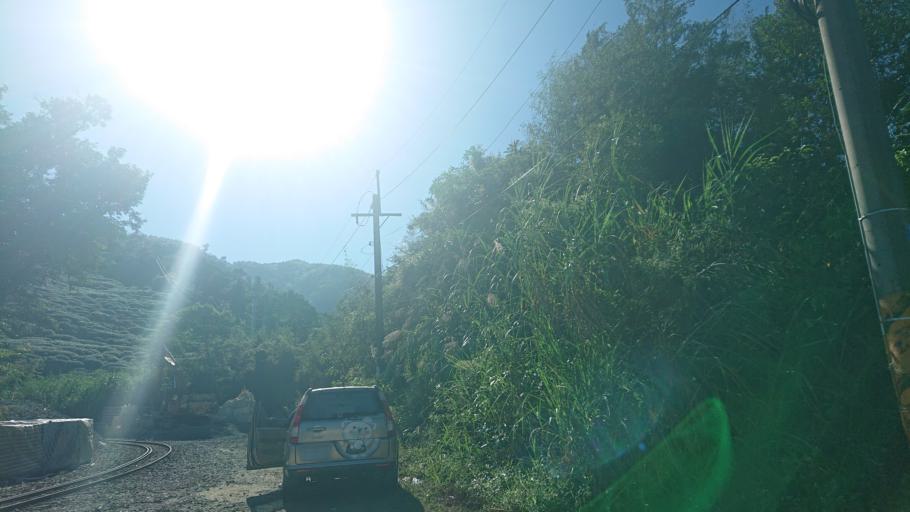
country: TW
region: Taiwan
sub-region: Chiayi
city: Jiayi Shi
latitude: 23.5358
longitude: 120.6285
